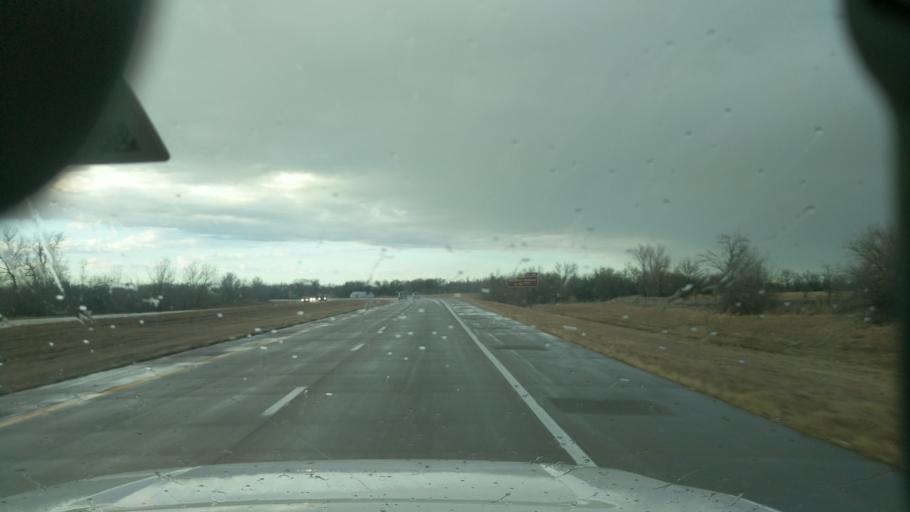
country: US
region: Kansas
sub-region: Harvey County
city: North Newton
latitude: 38.0758
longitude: -97.3300
